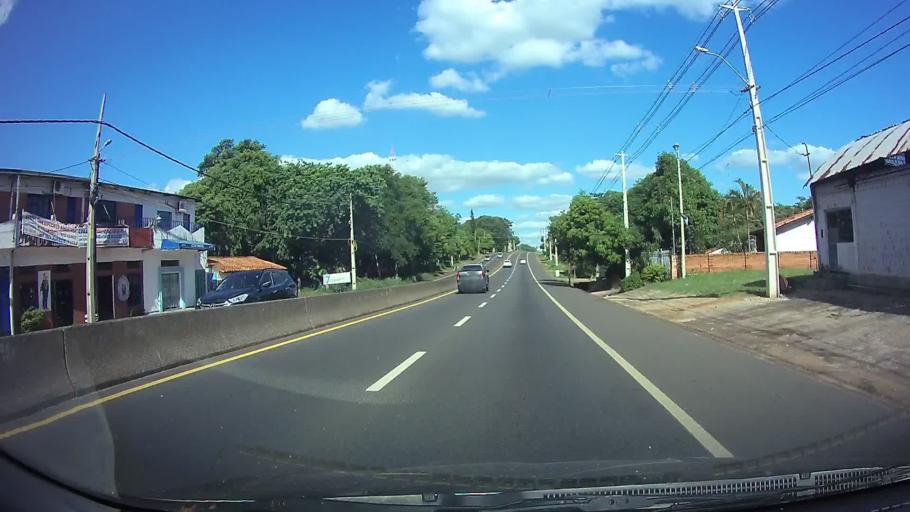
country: PY
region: Central
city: Itaugua
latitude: -25.3994
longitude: -57.3265
